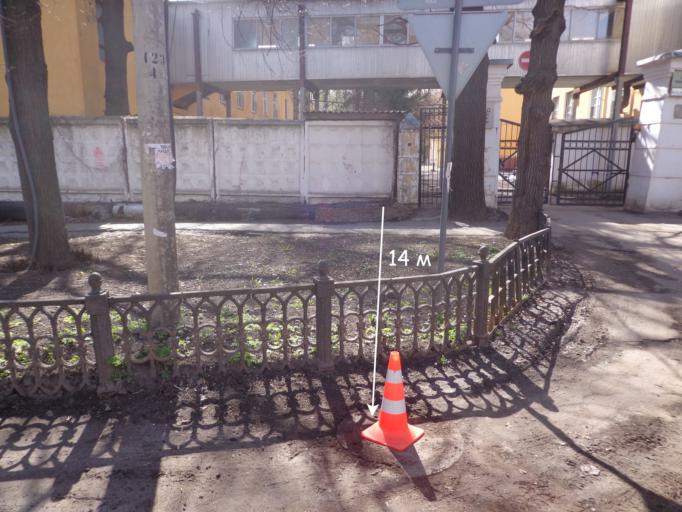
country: RU
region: Voronezj
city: Voronezh
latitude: 51.7196
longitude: 39.2211
